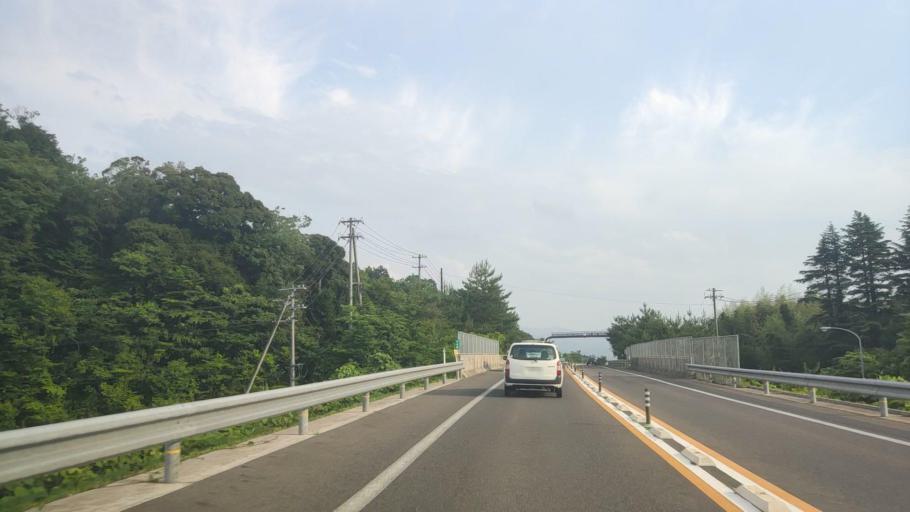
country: JP
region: Tottori
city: Kurayoshi
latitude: 35.4548
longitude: 133.8108
